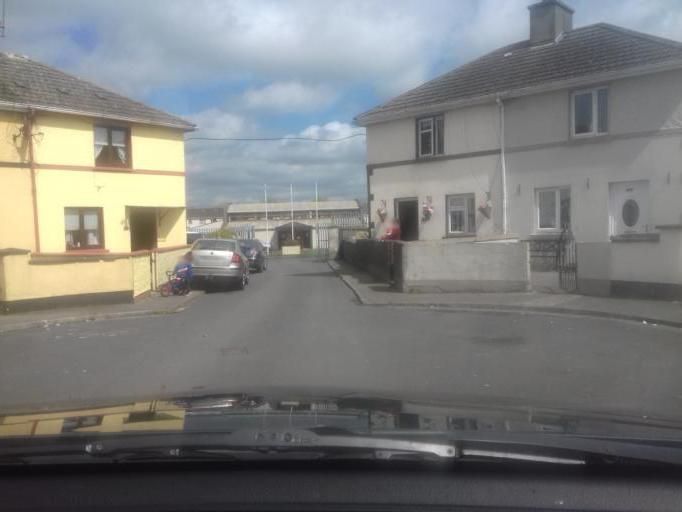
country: IE
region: Leinster
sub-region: Laois
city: Portlaoise
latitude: 53.0419
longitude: -7.3069
